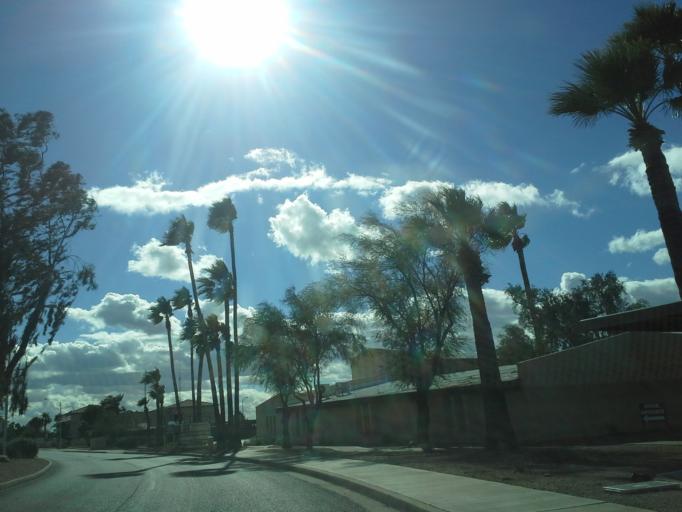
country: US
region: Arizona
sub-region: Maricopa County
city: Mesa
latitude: 33.4559
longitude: -111.7282
